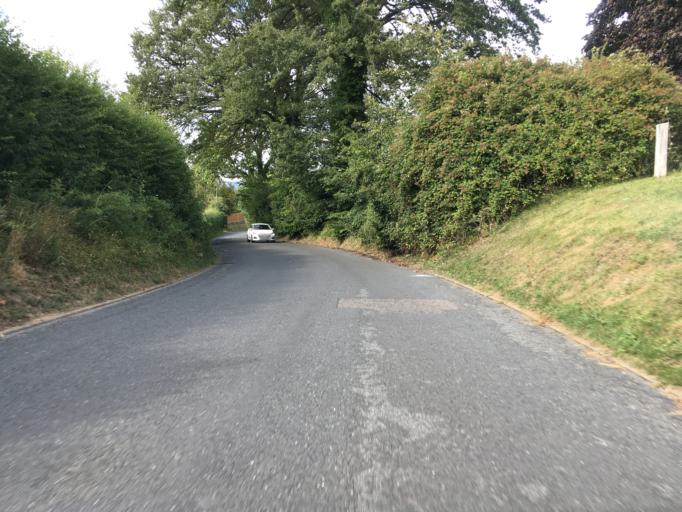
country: GB
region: England
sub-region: Kent
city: Maidstone
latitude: 51.2370
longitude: 0.5164
